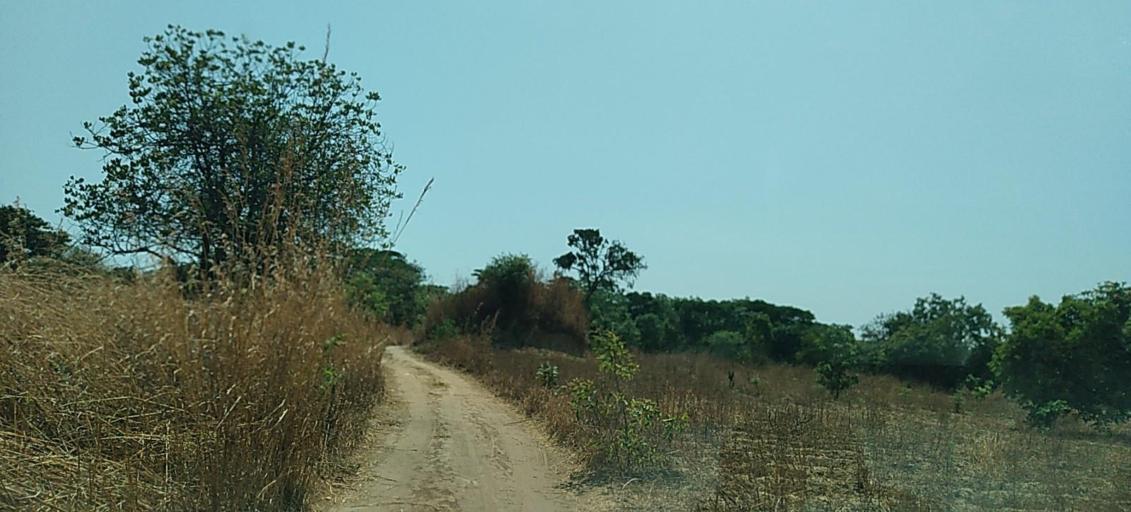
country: ZM
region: Copperbelt
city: Luanshya
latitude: -13.0071
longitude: 28.4758
